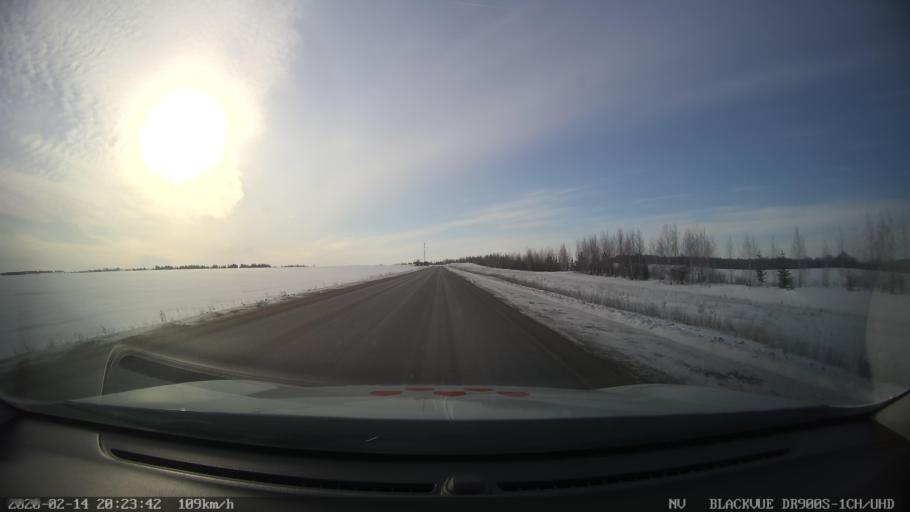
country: RU
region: Tatarstan
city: Verkhniy Uslon
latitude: 55.5239
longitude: 48.9694
